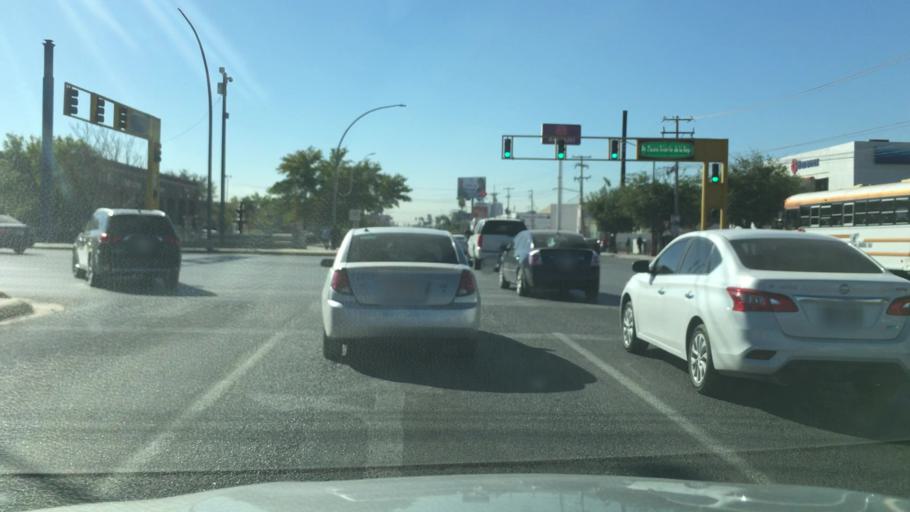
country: MX
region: Chihuahua
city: Ciudad Juarez
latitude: 31.7373
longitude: -106.4495
